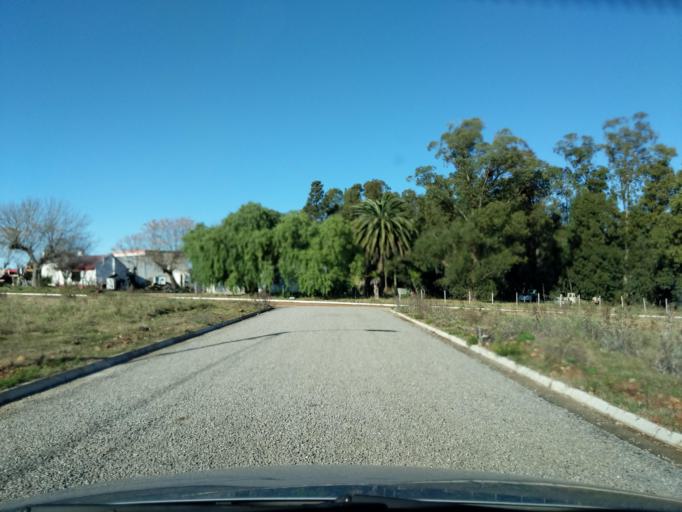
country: UY
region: Florida
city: Florida
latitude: -34.0872
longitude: -56.2398
